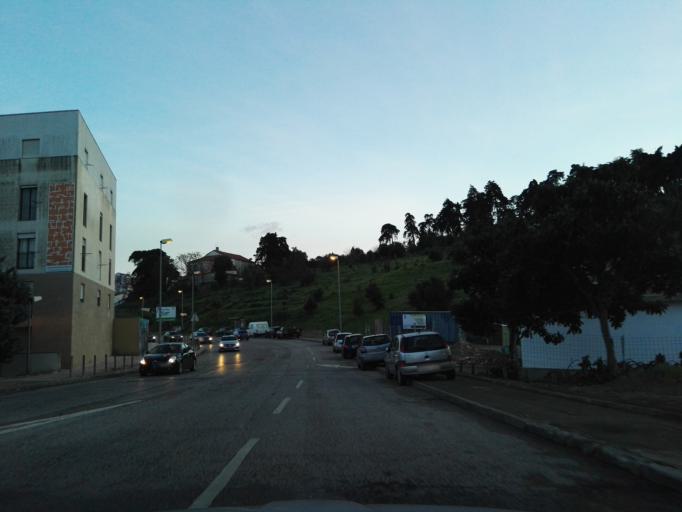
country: PT
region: Lisbon
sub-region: Odivelas
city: Pontinha
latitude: 38.7360
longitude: -9.1722
